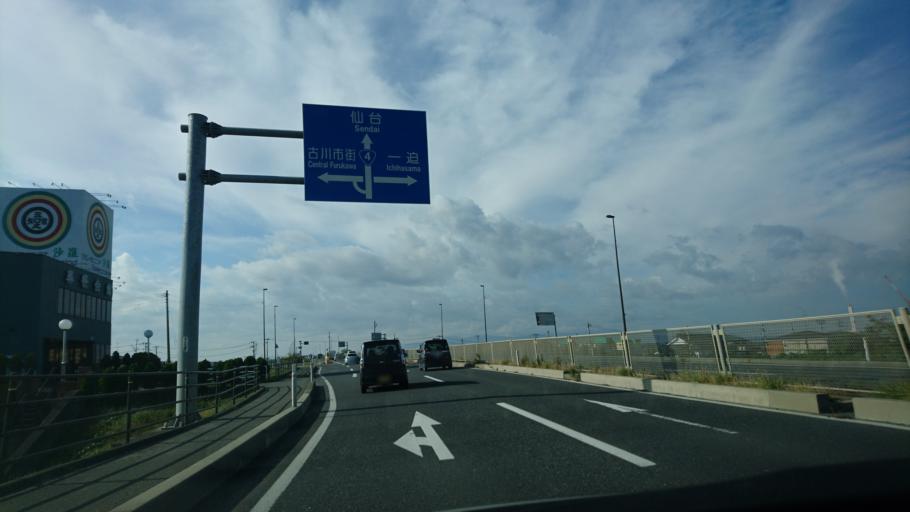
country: JP
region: Miyagi
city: Furukawa
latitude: 38.5983
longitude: 140.9688
